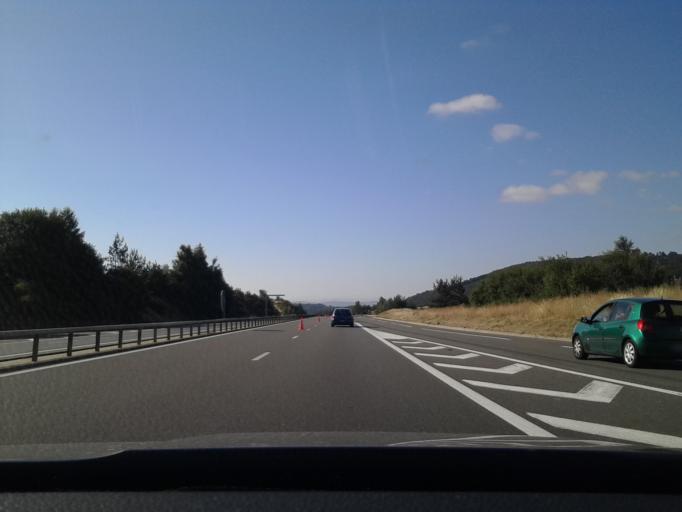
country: FR
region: Languedoc-Roussillon
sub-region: Departement de la Lozere
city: Marvejols
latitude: 44.6317
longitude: 3.2420
